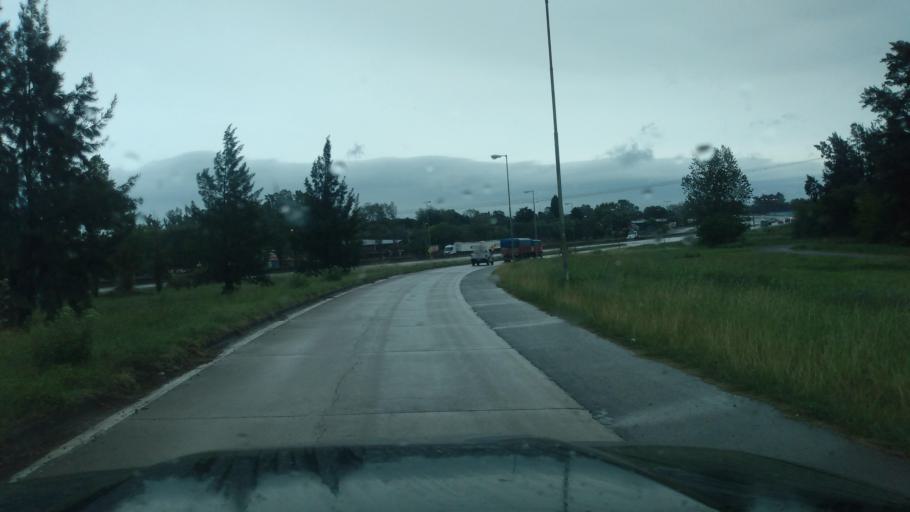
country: AR
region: Buenos Aires
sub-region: Partido de Pilar
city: Pilar
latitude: -34.3939
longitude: -59.0231
